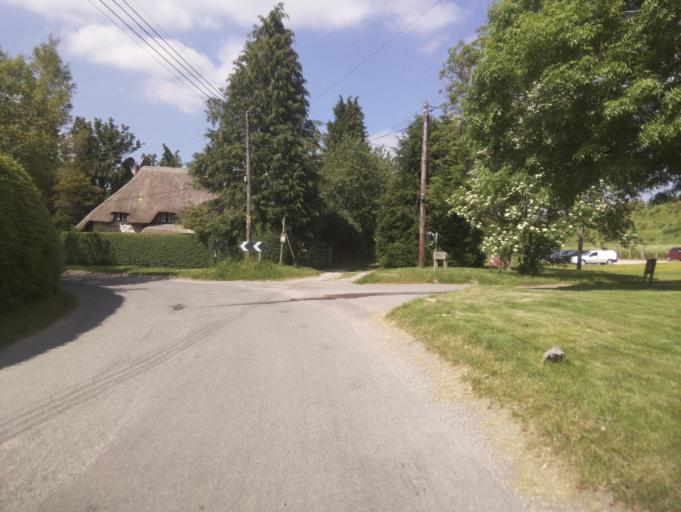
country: GB
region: England
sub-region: Wiltshire
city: Rushall
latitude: 51.2751
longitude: -1.7995
